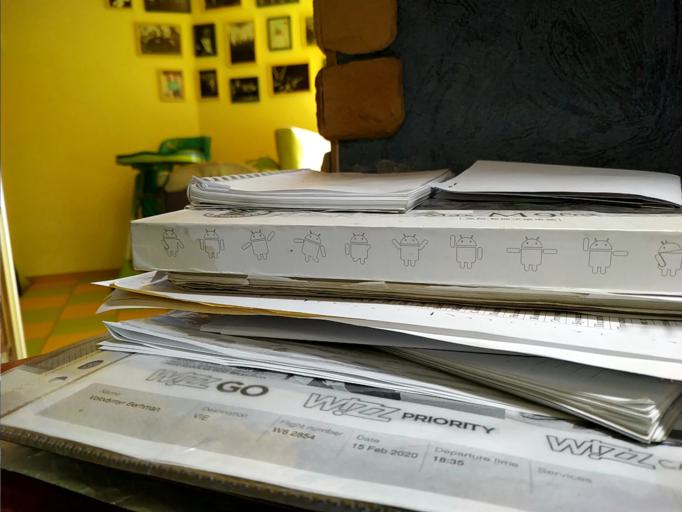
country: RU
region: Pskov
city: Plyussa
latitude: 58.6667
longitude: 29.3220
